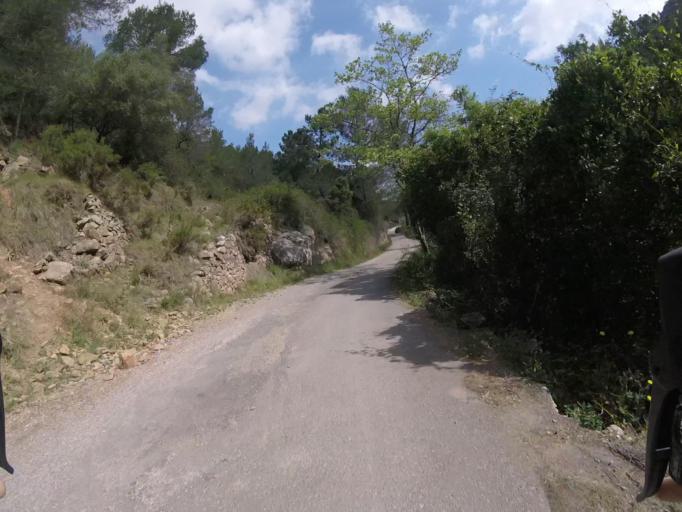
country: ES
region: Valencia
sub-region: Provincia de Castello
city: Cabanes
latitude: 40.1084
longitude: 0.0417
